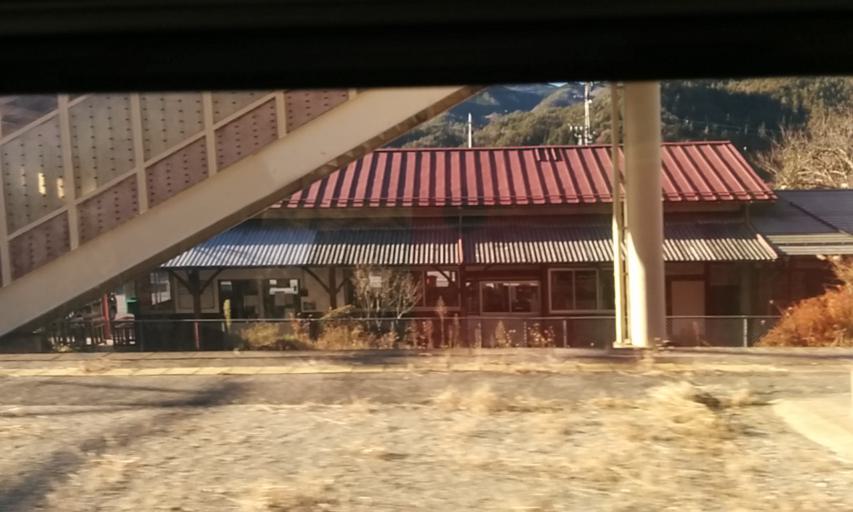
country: JP
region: Nagano
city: Iida
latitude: 35.6973
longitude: 137.6944
